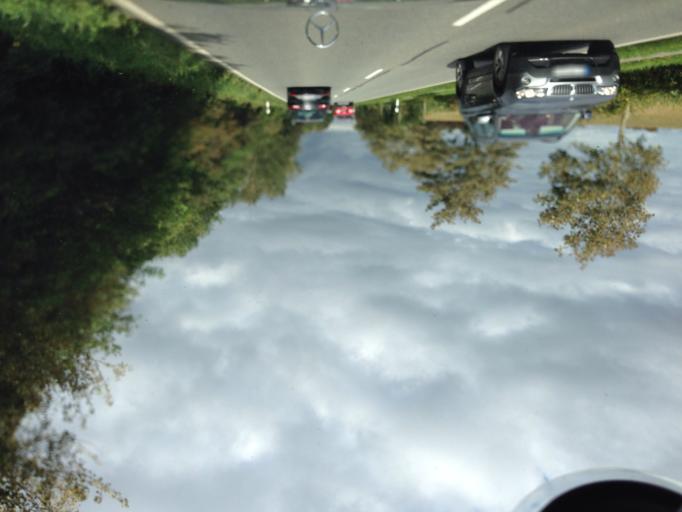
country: DE
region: Schleswig-Holstein
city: Leck
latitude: 54.7440
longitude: 8.9599
